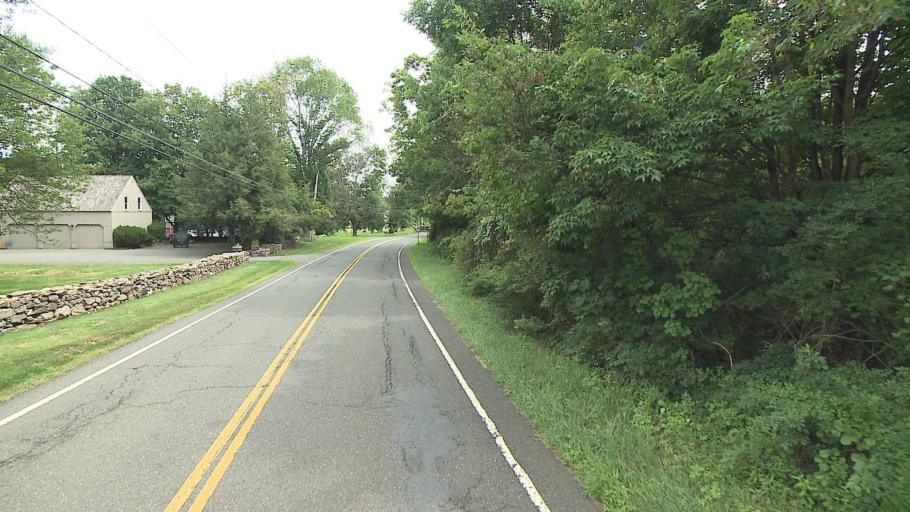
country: US
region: Connecticut
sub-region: Litchfield County
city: Woodbury
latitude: 41.5424
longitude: -73.2350
